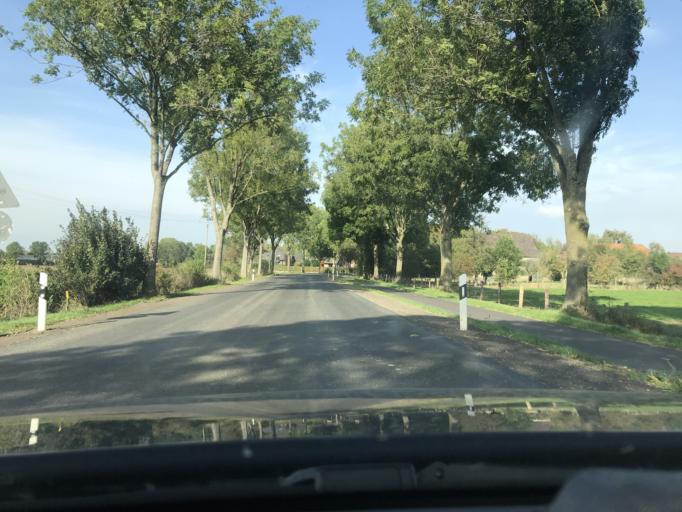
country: DE
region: North Rhine-Westphalia
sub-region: Regierungsbezirk Dusseldorf
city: Emmerich
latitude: 51.7861
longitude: 6.2319
